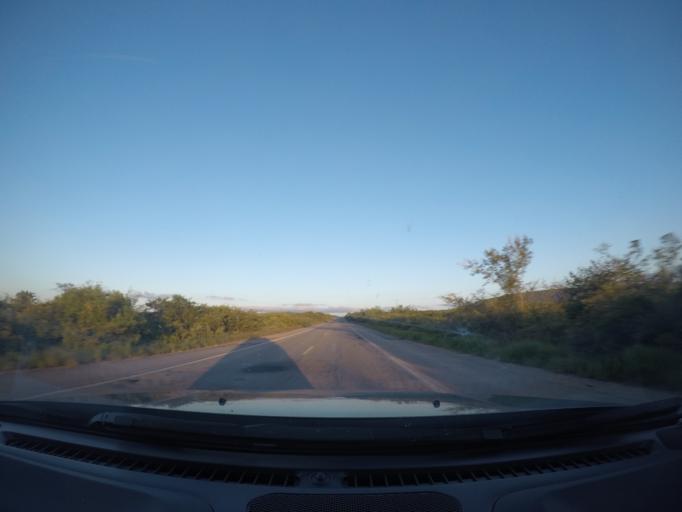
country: BR
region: Bahia
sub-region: Seabra
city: Seabra
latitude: -12.3912
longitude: -41.9079
